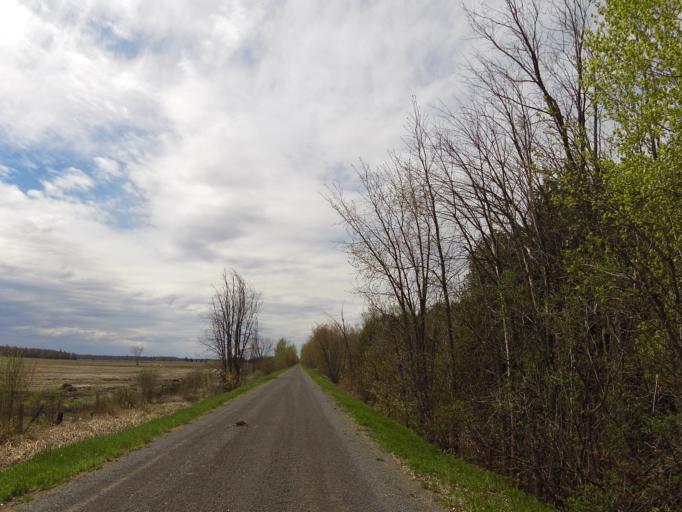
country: CA
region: Ontario
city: Hawkesbury
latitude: 45.5370
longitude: -74.7183
